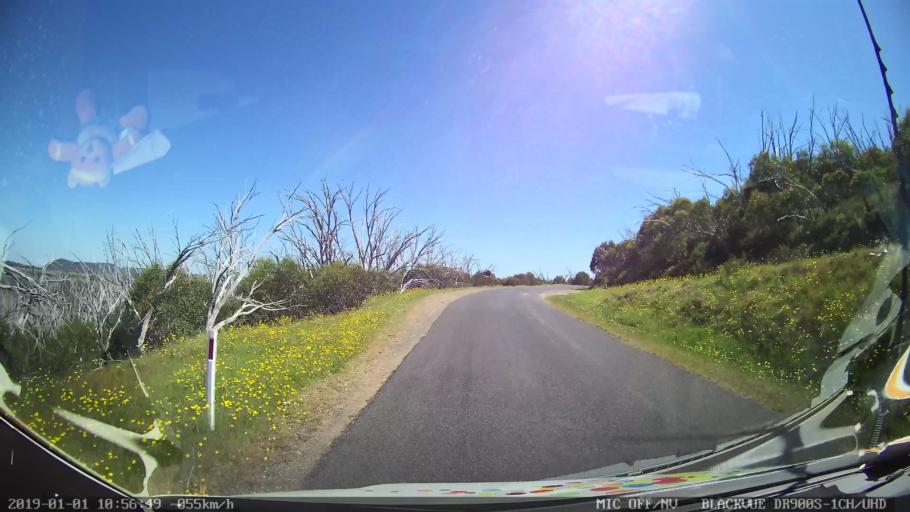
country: AU
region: New South Wales
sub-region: Snowy River
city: Jindabyne
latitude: -36.0017
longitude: 148.3941
